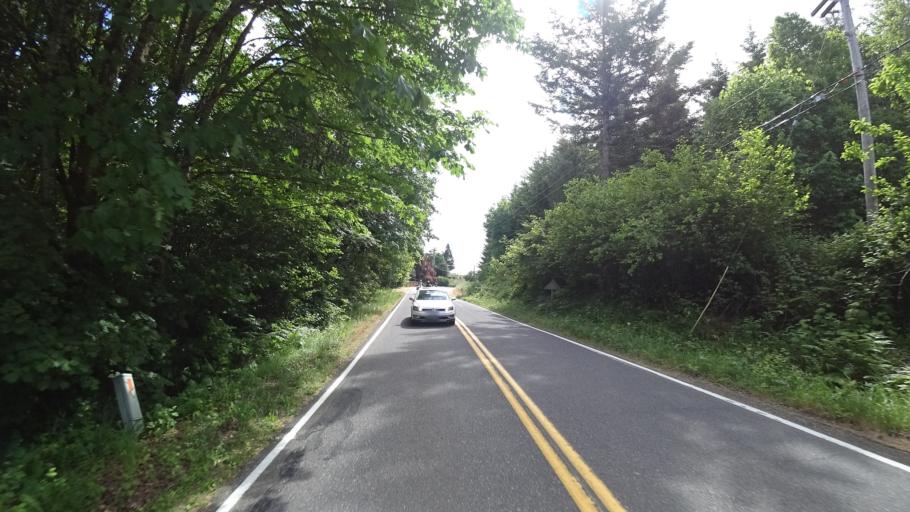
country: US
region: Oregon
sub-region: Washington County
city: Bethany
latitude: 45.6072
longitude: -122.8361
